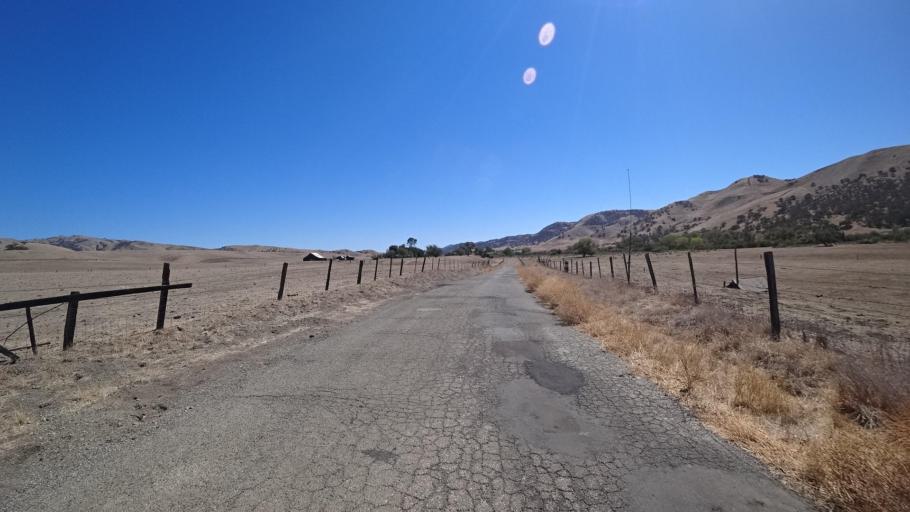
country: US
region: California
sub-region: Monterey County
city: King City
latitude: 36.2852
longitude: -120.9645
